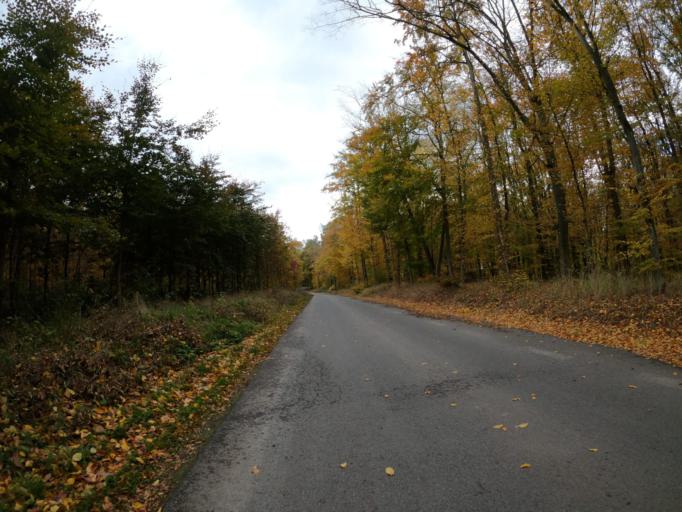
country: PL
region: West Pomeranian Voivodeship
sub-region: Powiat mysliborski
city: Barlinek
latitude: 52.9442
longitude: 15.2832
